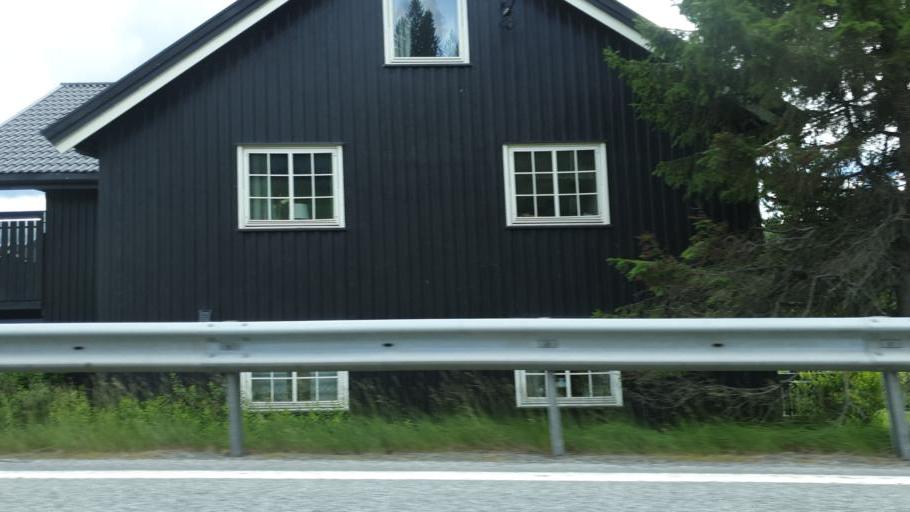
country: NO
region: Sor-Trondelag
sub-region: Rennebu
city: Berkak
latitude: 62.8791
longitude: 10.0907
